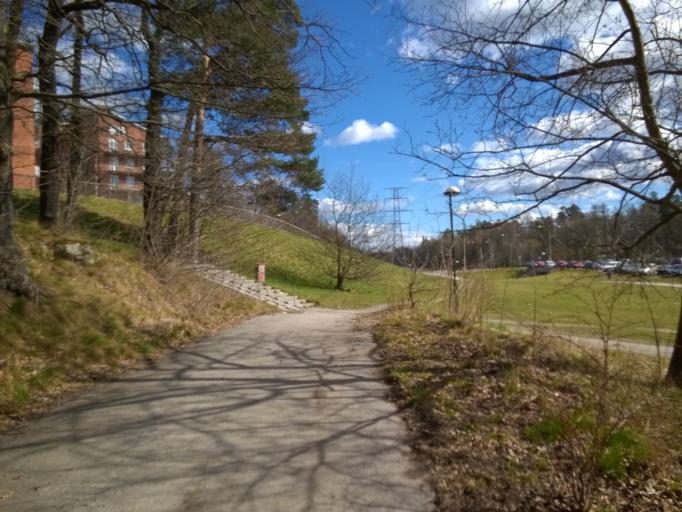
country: SE
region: Stockholm
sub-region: Norrtalje Kommun
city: Bergshamra
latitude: 59.3701
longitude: 18.0582
